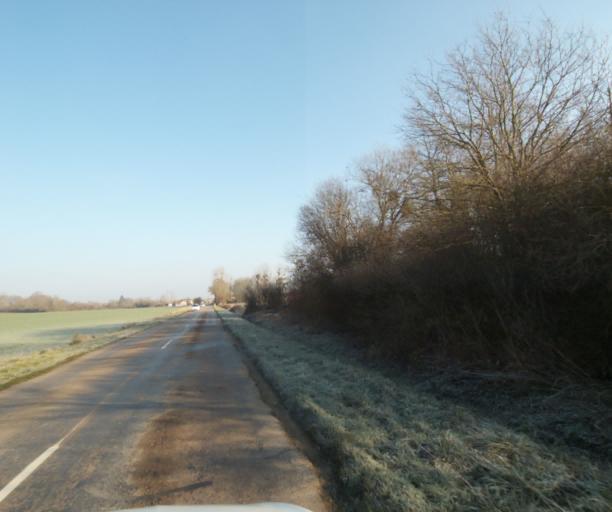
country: FR
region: Champagne-Ardenne
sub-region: Departement de la Haute-Marne
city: Montier-en-Der
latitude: 48.4497
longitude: 4.7648
